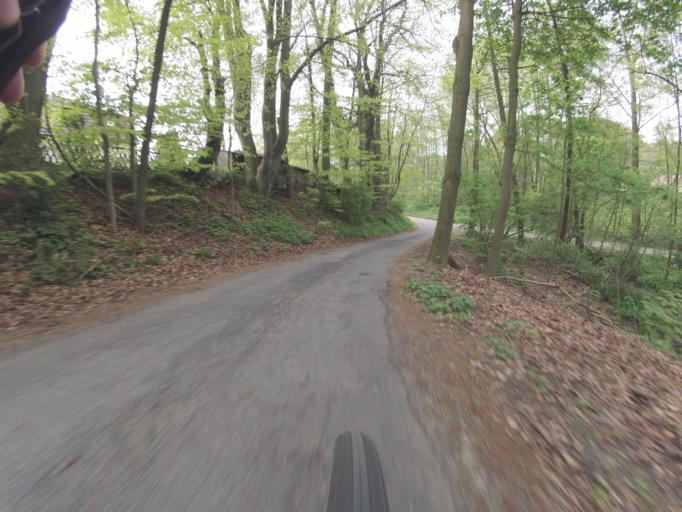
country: DE
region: North Rhine-Westphalia
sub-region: Regierungsbezirk Munster
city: Mettingen
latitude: 52.3075
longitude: 7.7901
